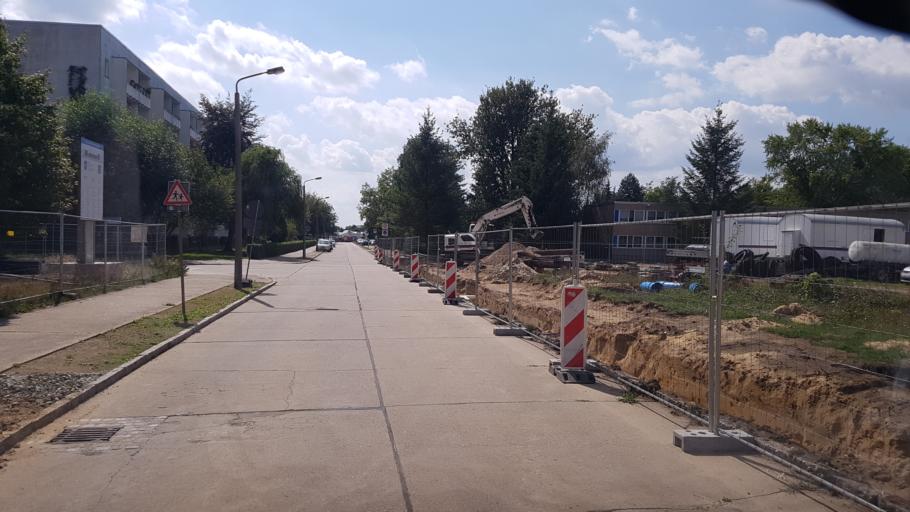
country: DE
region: Brandenburg
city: Lubbenau
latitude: 51.8638
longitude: 13.9372
